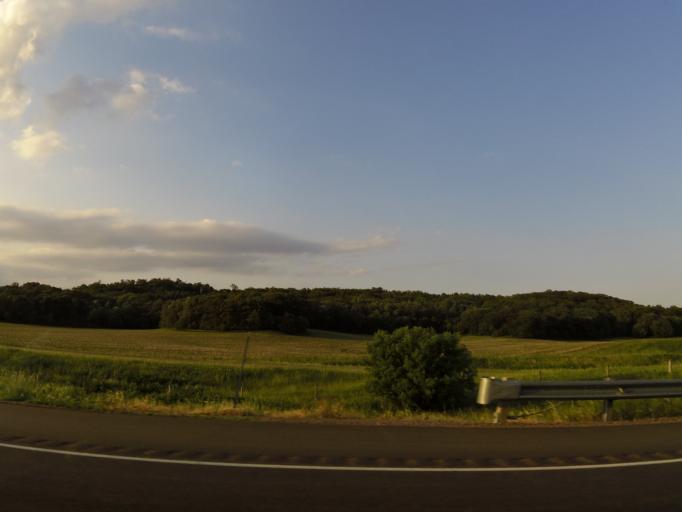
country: US
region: Wisconsin
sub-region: Jackson County
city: Black River Falls
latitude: 44.4087
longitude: -91.0334
